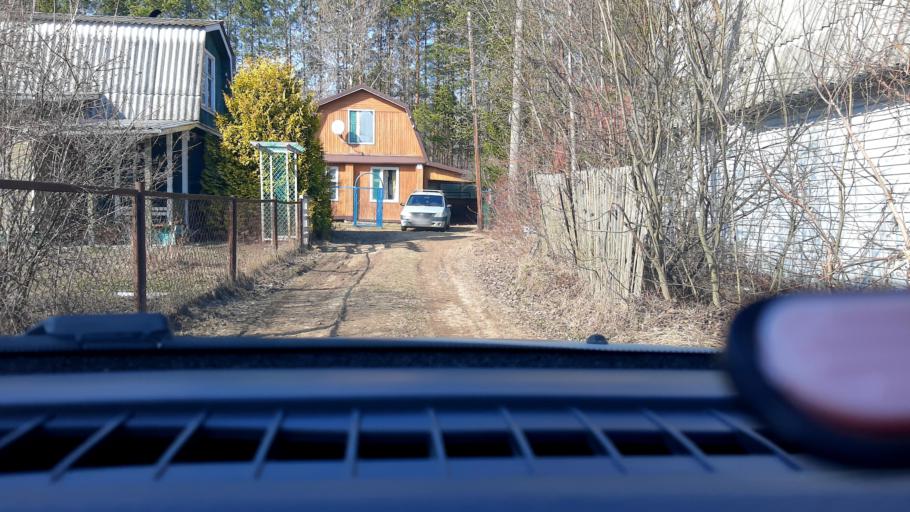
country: RU
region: Nizjnij Novgorod
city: Neklyudovo
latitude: 56.4282
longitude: 43.9260
